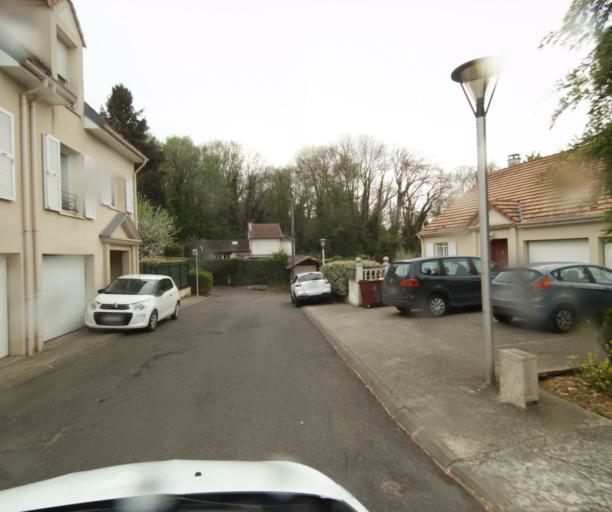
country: FR
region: Ile-de-France
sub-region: Departement de Seine-et-Marne
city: Torcy
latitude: 48.8566
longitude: 2.6420
